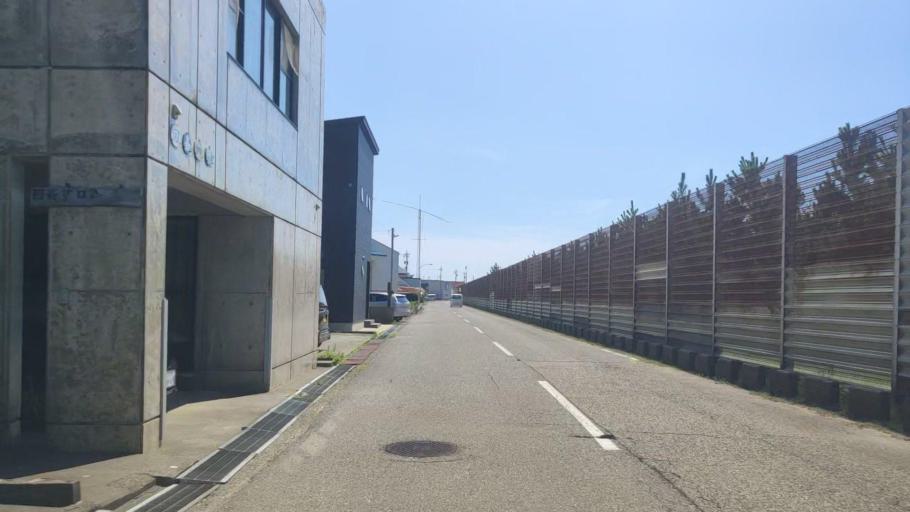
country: JP
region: Ishikawa
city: Kanazawa-shi
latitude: 36.6062
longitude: 136.5922
